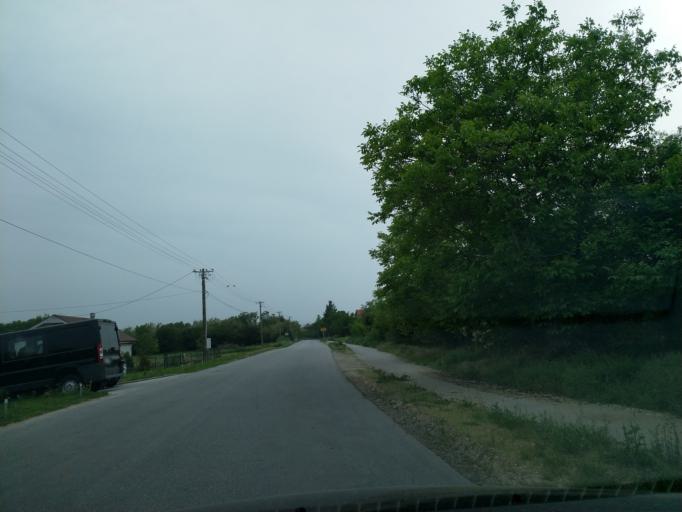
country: RS
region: Central Serbia
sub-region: Pomoravski Okrug
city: Jagodina
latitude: 43.9693
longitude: 21.2349
